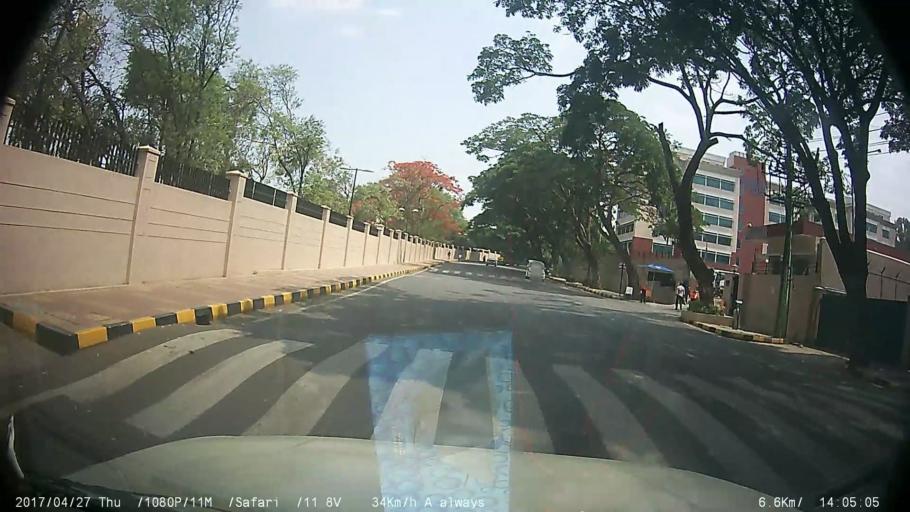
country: IN
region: Karnataka
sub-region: Bangalore Urban
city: Anekal
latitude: 12.8431
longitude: 77.6604
